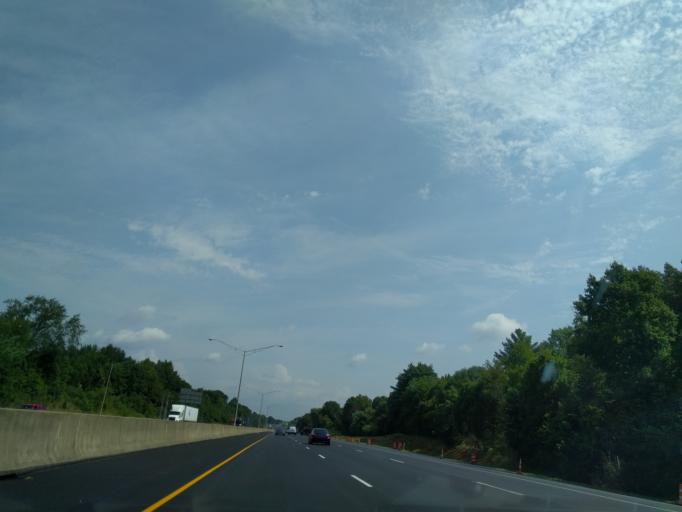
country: US
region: Kentucky
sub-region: Warren County
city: Bowling Green
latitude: 36.9803
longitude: -86.3896
